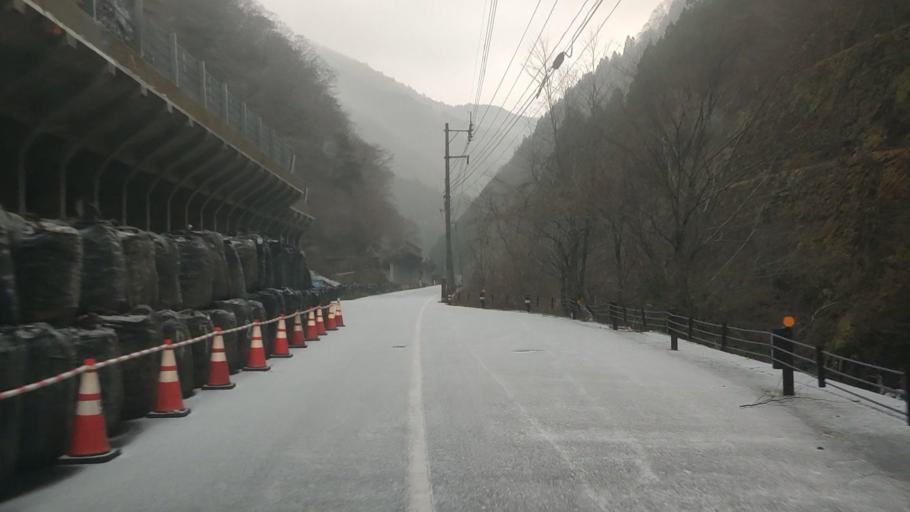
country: JP
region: Kumamoto
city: Matsubase
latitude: 32.5546
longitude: 130.9273
